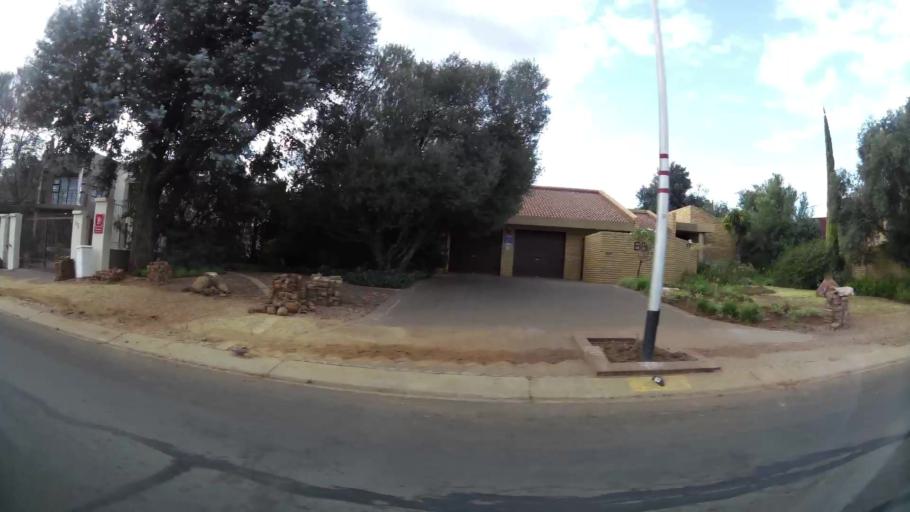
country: ZA
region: Orange Free State
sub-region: Mangaung Metropolitan Municipality
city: Bloemfontein
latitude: -29.0807
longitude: 26.1998
